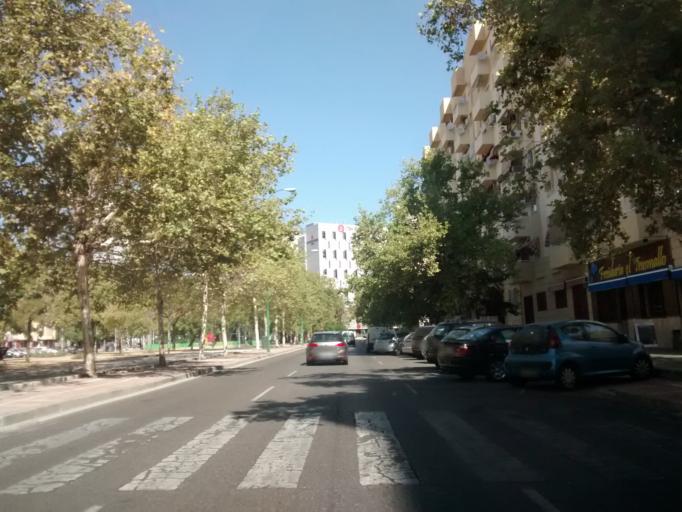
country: ES
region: Andalusia
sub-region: Provincia de Sevilla
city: Sevilla
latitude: 37.3737
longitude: -5.9744
